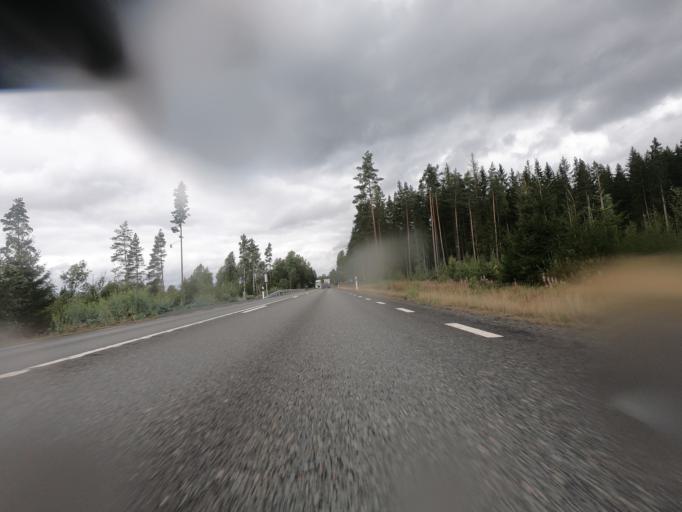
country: SE
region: Joenkoeping
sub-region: Savsjo Kommun
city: Vrigstad
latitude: 57.4323
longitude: 14.3199
